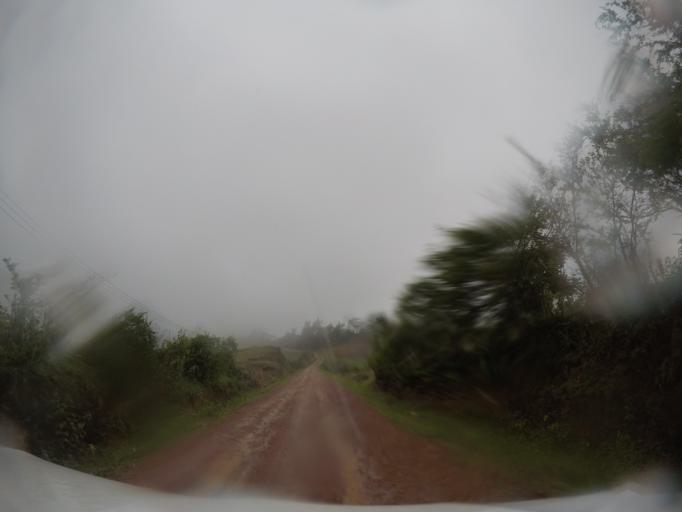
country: TL
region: Baucau
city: Venilale
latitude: -8.6374
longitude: 126.4097
